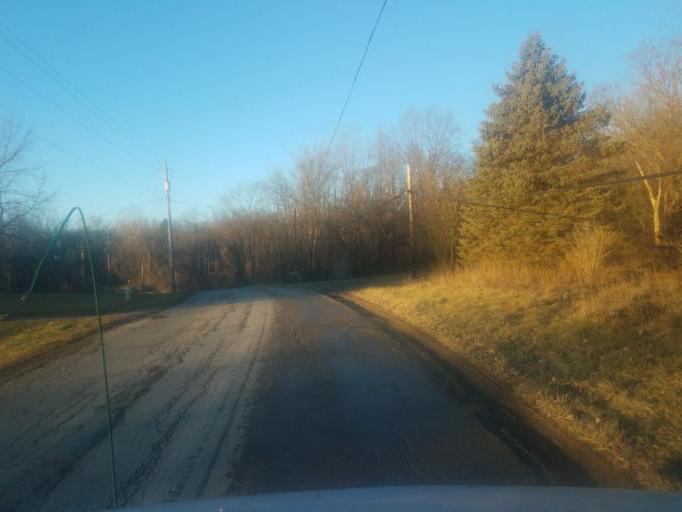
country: US
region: Ohio
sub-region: Richland County
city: Mansfield
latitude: 40.8015
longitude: -82.5358
